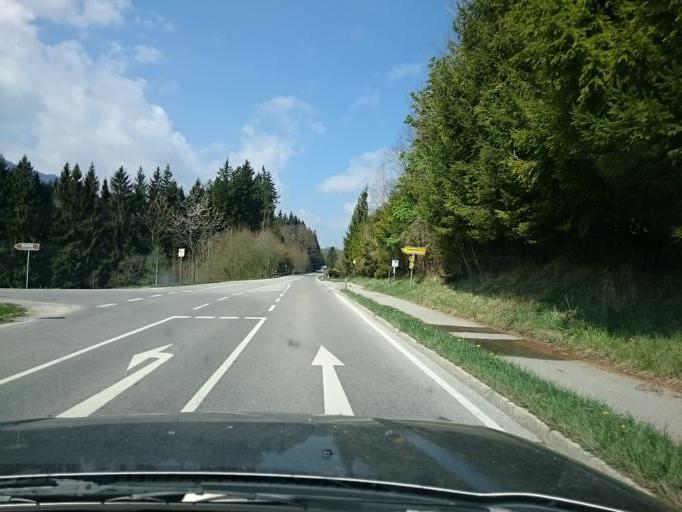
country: DE
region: Bavaria
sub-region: Upper Bavaria
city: Uffing
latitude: 47.6672
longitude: 11.1330
